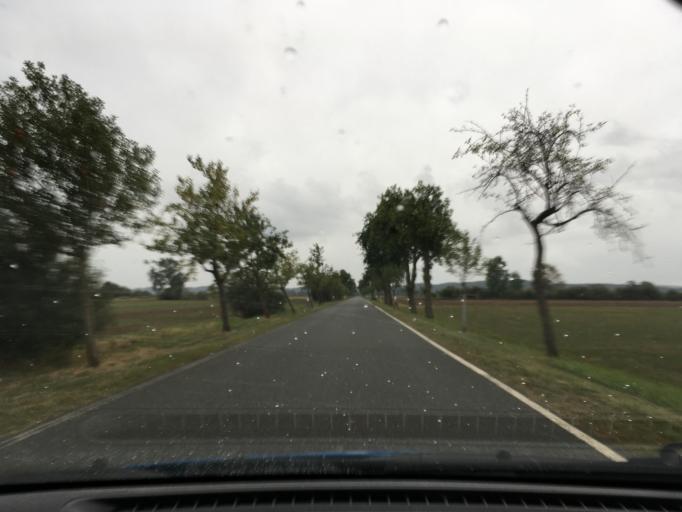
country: DE
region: Lower Saxony
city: Hitzacker
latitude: 53.2209
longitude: 10.9874
